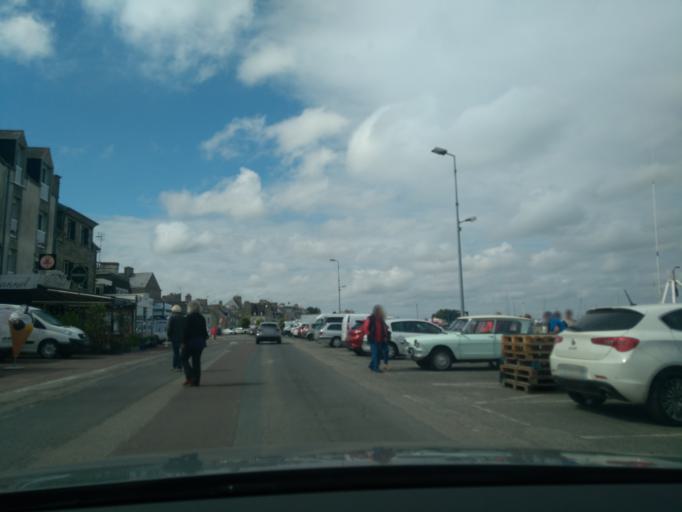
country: FR
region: Lower Normandy
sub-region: Departement de la Manche
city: Saint-Vaast-la-Hougue
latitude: 49.5877
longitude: -1.2654
